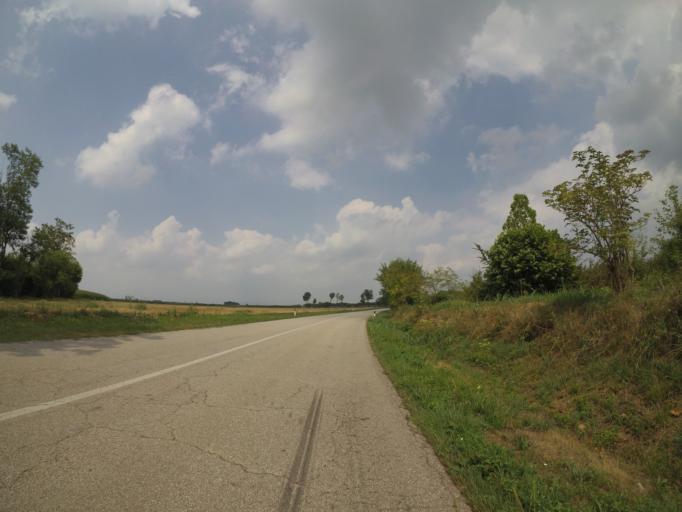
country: IT
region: Friuli Venezia Giulia
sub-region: Provincia di Udine
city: Sedegliano
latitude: 46.0092
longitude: 13.0047
